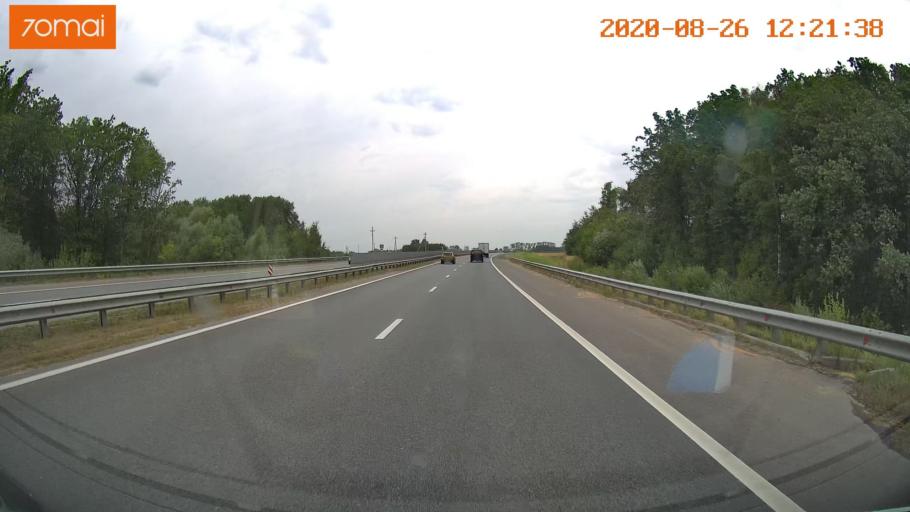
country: RU
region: Rjazan
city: Murmino
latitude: 54.4999
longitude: 39.9562
